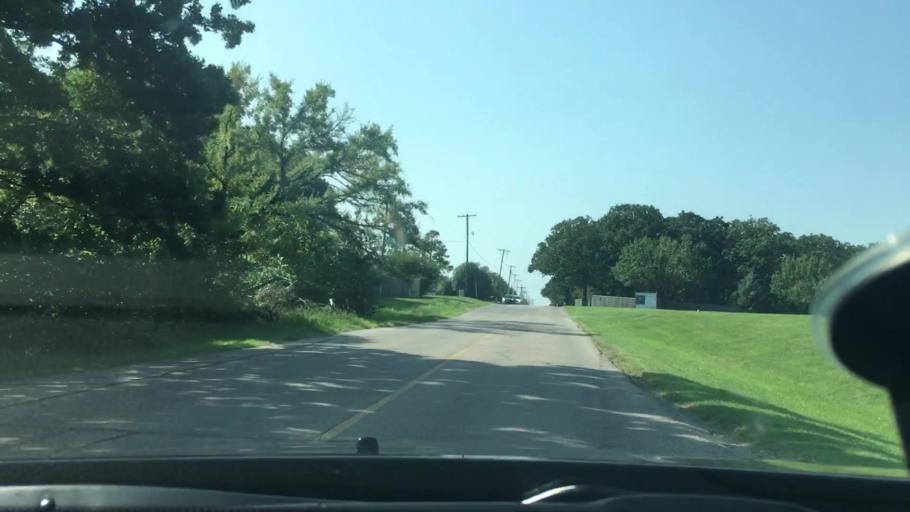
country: US
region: Oklahoma
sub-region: Bryan County
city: Durant
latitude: 34.0119
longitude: -96.3905
